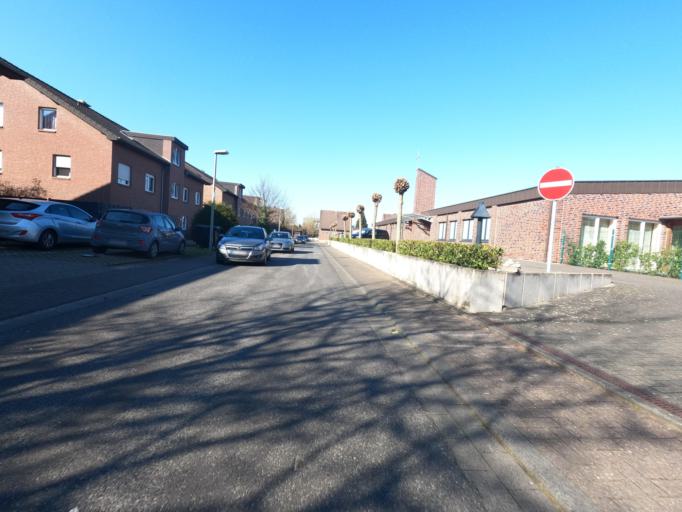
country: DE
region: North Rhine-Westphalia
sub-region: Regierungsbezirk Koln
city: Linnich
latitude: 51.0306
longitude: 6.2820
